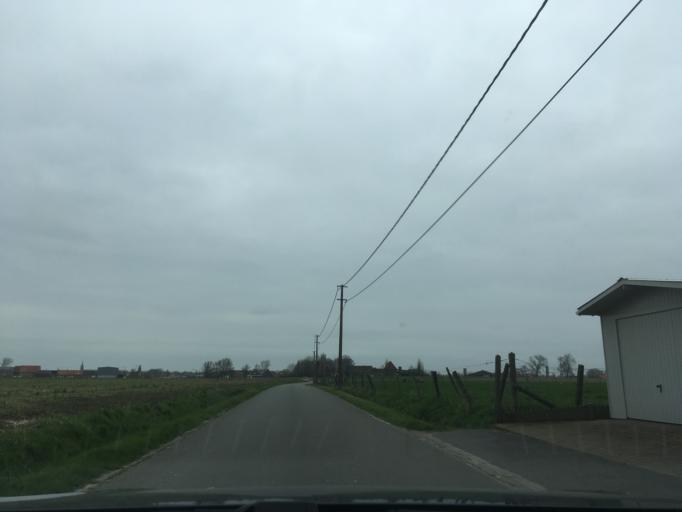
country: BE
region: Flanders
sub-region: Provincie West-Vlaanderen
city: Lichtervelde
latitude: 51.0090
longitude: 3.1525
